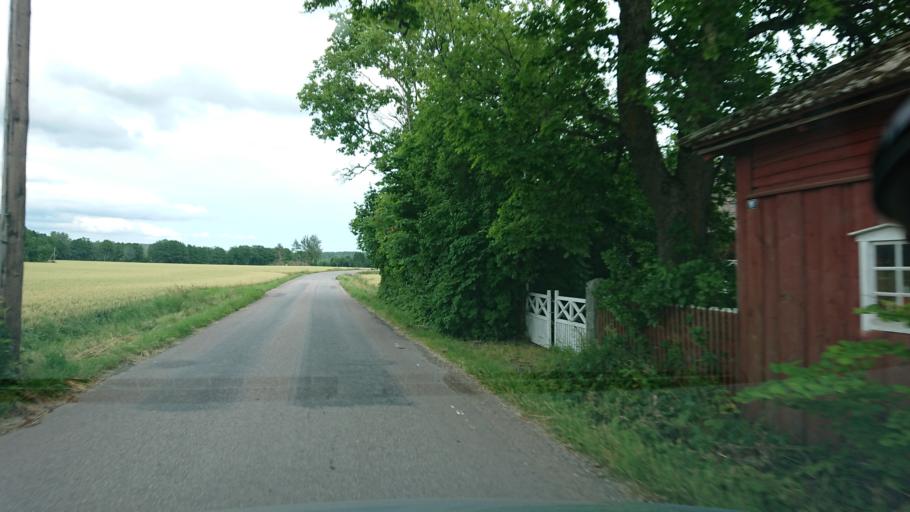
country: SE
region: Uppsala
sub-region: Osthammars Kommun
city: Bjorklinge
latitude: 59.9901
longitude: 17.5370
